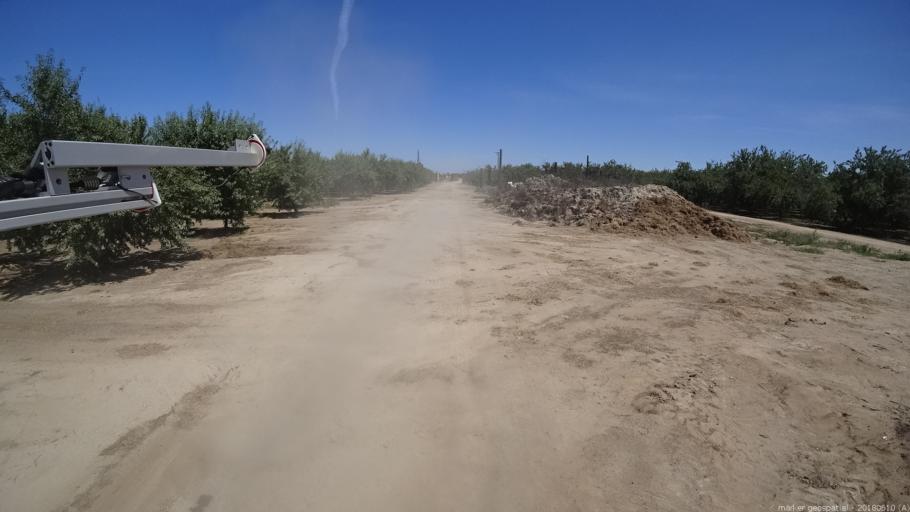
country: US
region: California
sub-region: Madera County
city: Chowchilla
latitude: 37.0386
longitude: -120.4194
